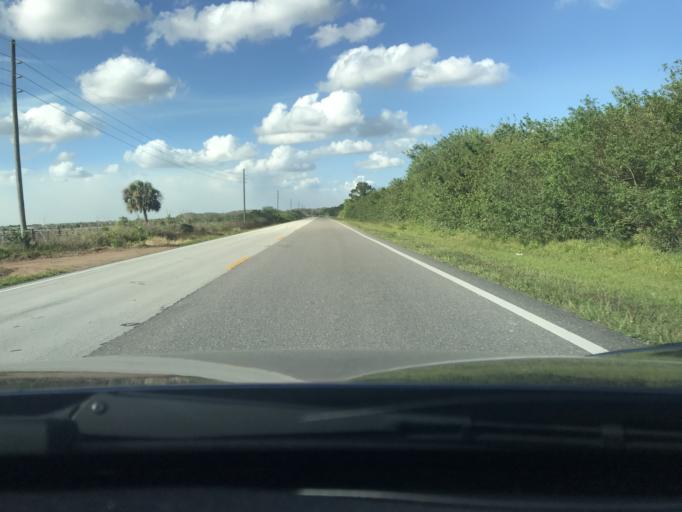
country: US
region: Florida
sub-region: Okeechobee County
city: Taylor Creek
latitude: 27.2787
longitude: -80.6956
